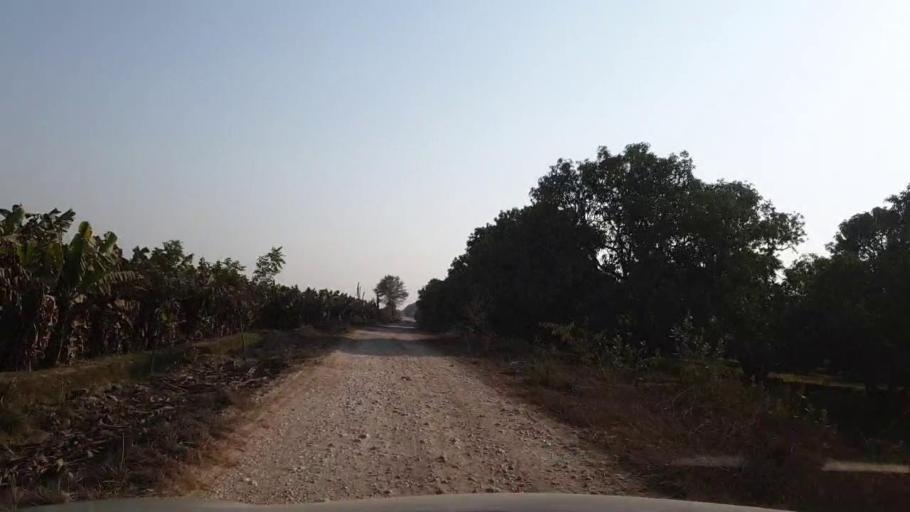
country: PK
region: Sindh
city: Tando Allahyar
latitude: 25.5772
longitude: 68.7643
